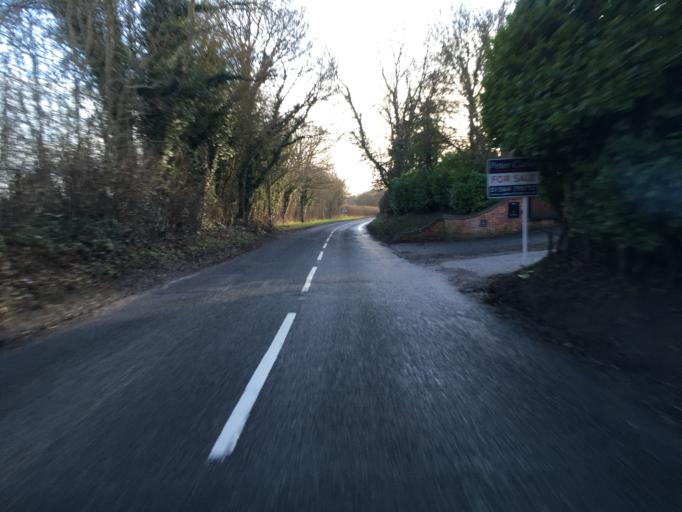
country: GB
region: England
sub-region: Warwickshire
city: Henley in Arden
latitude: 52.2617
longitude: -1.7852
